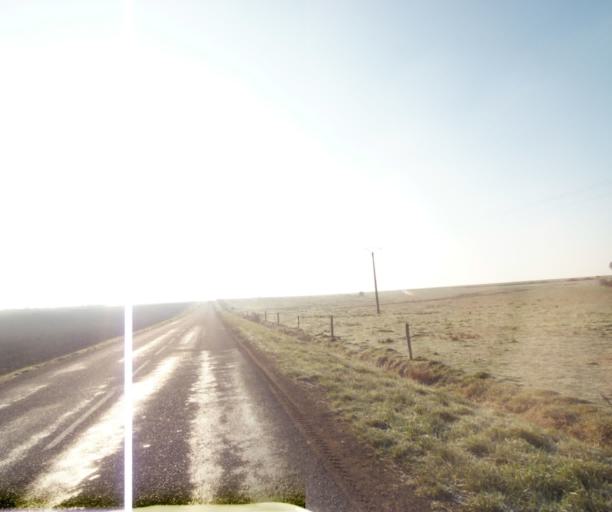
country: FR
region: Champagne-Ardenne
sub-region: Departement de la Haute-Marne
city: Montier-en-Der
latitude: 48.5036
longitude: 4.7495
